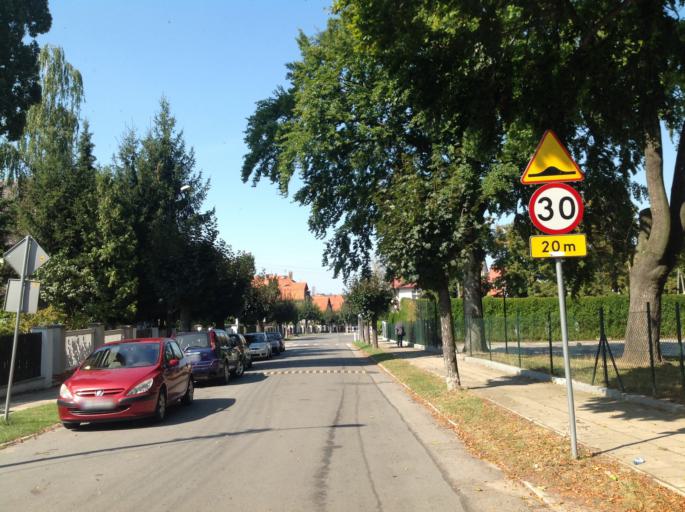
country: PL
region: Lower Silesian Voivodeship
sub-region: Powiat zabkowicki
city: Ziebice
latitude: 50.5968
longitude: 17.0461
